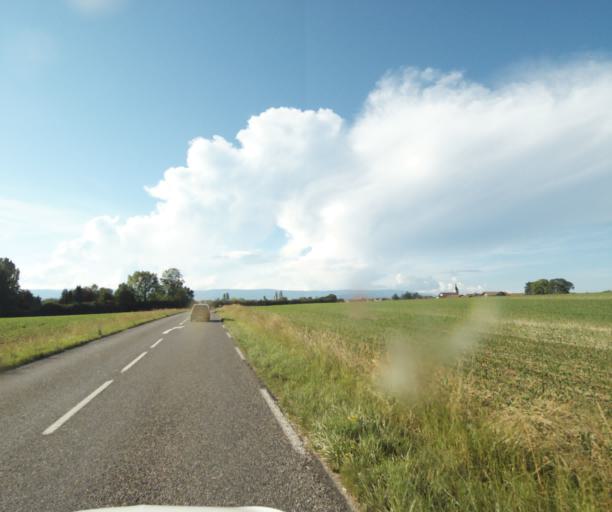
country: FR
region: Rhone-Alpes
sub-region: Departement de la Haute-Savoie
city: Messery
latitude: 46.3454
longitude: 6.2916
